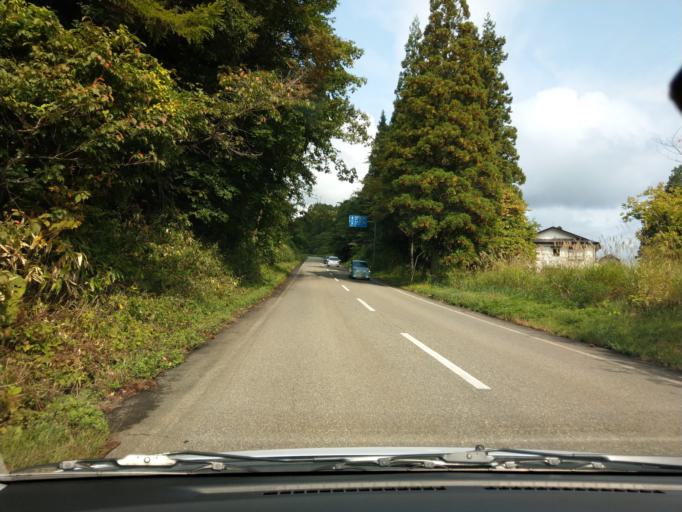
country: JP
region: Akita
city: Omagari
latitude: 39.4664
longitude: 140.3178
